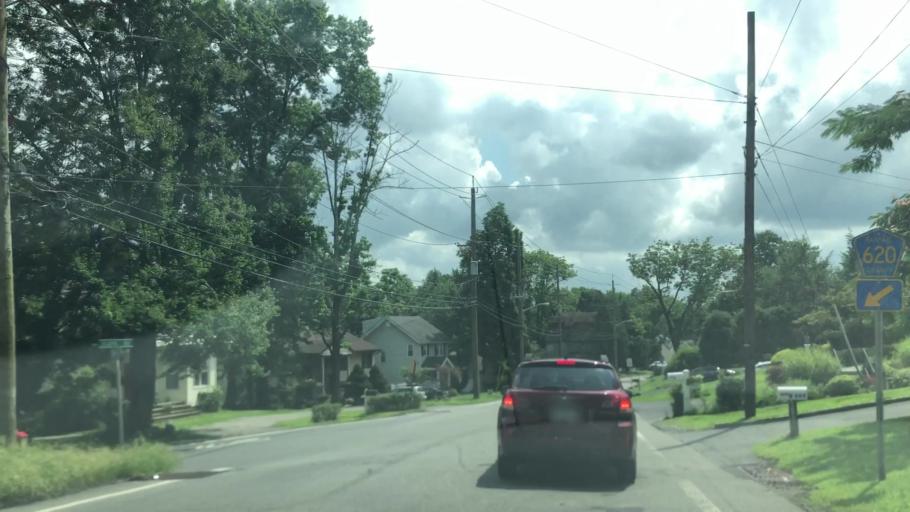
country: US
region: New Jersey
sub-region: Passaic County
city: Little Falls
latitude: 40.8625
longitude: -74.2021
